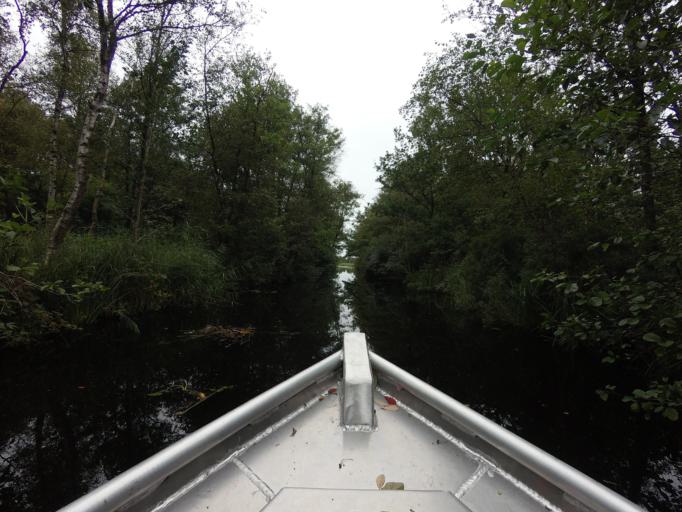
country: NL
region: Overijssel
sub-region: Gemeente Steenwijkerland
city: Oldemarkt
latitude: 52.7954
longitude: 5.9429
